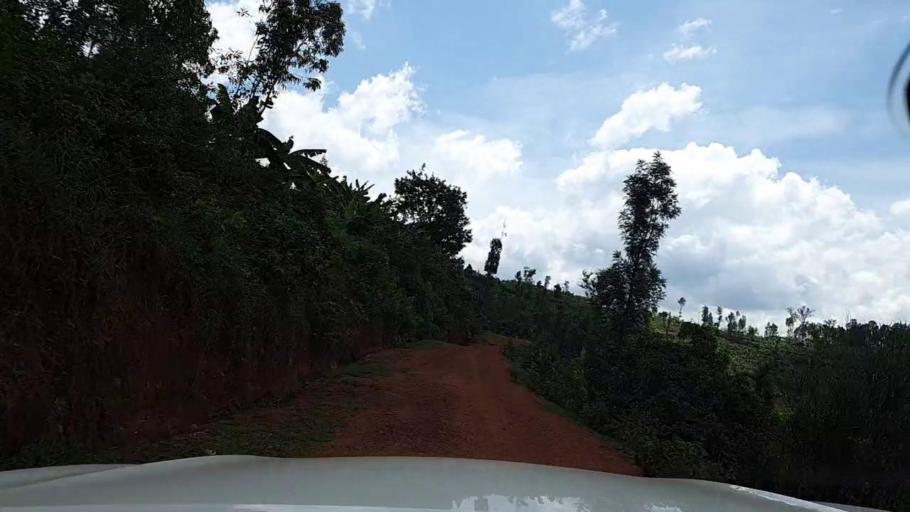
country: RW
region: Southern Province
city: Butare
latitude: -2.7486
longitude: 29.7623
